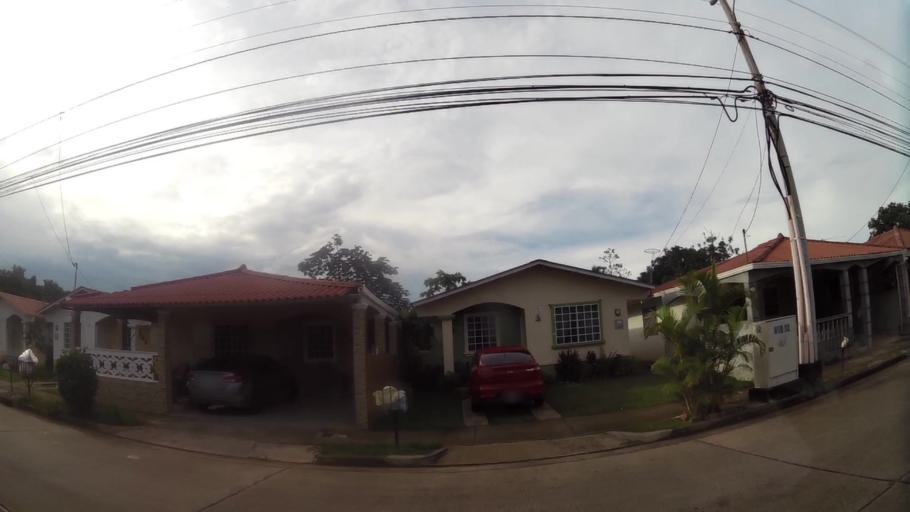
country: PA
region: Panama
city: La Chorrera
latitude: 8.8840
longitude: -79.7597
